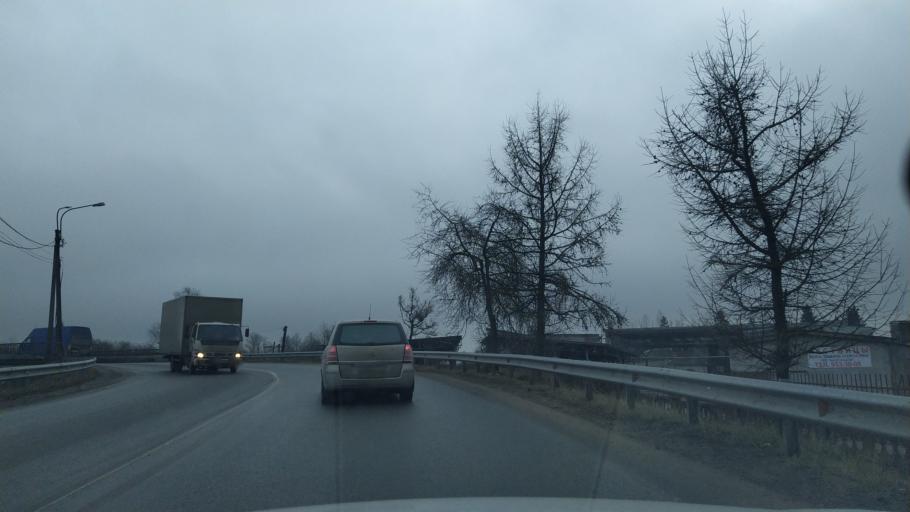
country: RU
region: St.-Petersburg
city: Krasnoye Selo
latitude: 59.7292
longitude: 30.1028
